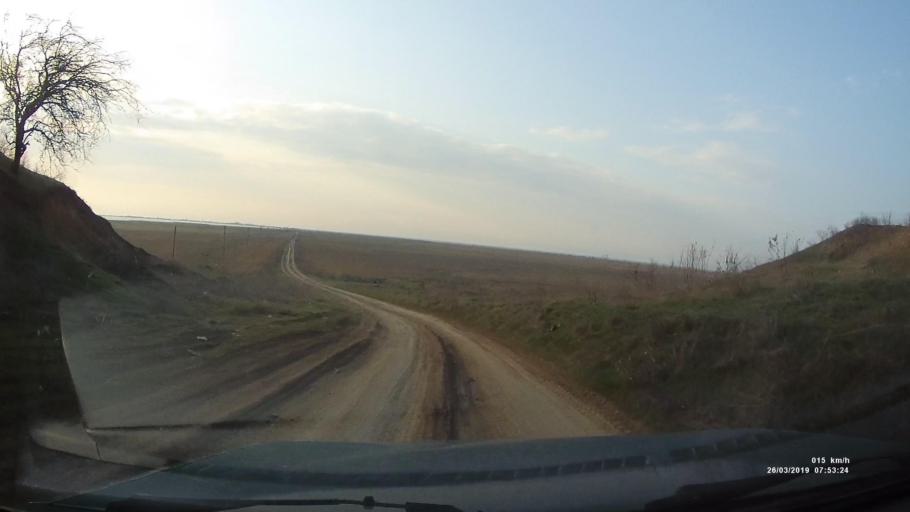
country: RU
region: Krasnodarskiy
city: Shabel'skoye
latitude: 47.1357
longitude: 38.5487
